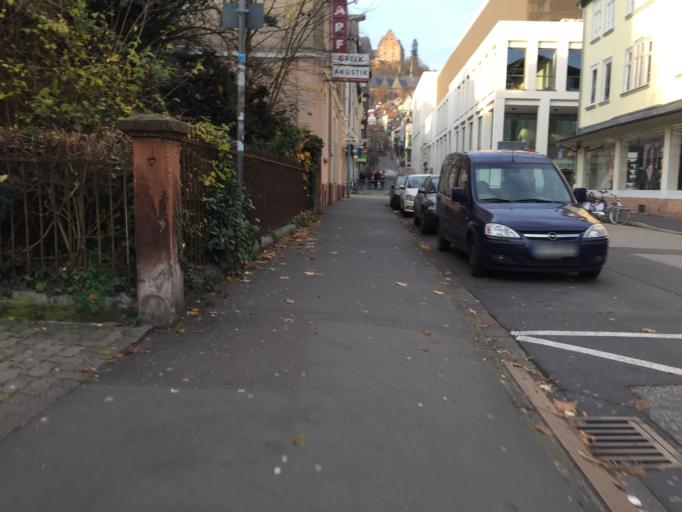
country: DE
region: Hesse
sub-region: Regierungsbezirk Giessen
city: Marburg an der Lahn
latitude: 50.8057
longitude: 8.7691
